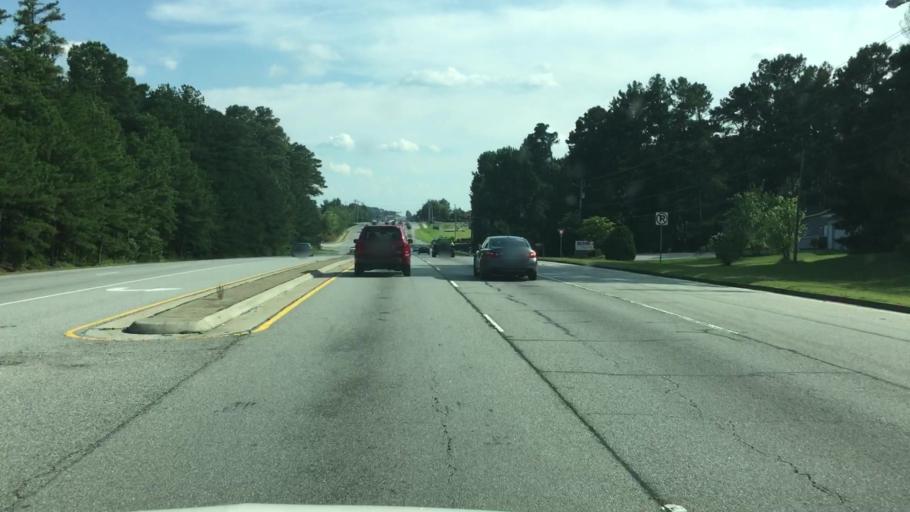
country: US
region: Georgia
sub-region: Gwinnett County
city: Snellville
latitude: 33.8928
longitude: -84.0079
